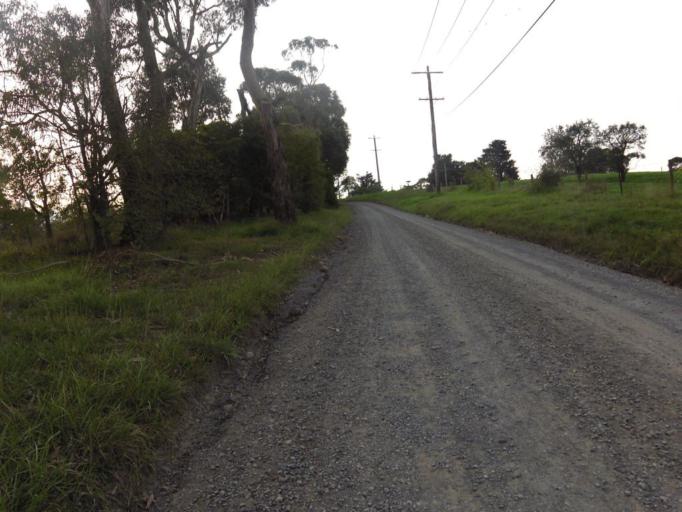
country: AU
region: Victoria
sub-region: Yarra Ranges
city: Belgrave South
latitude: -37.9204
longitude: 145.3251
